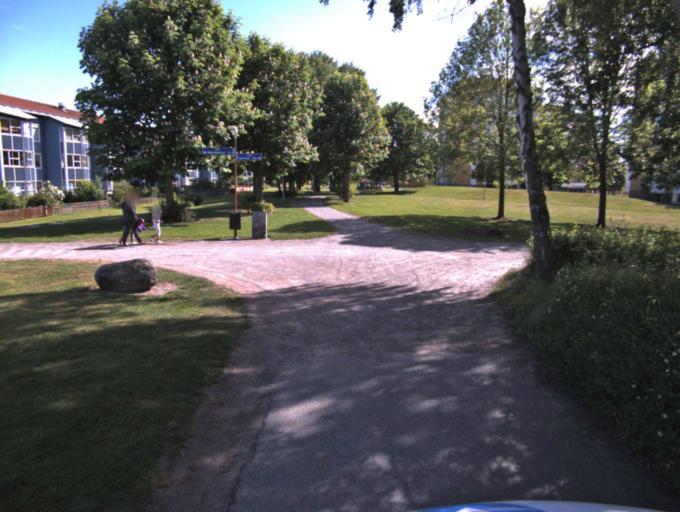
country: SE
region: Skane
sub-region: Kristianstads Kommun
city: Kristianstad
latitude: 56.0419
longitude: 14.1832
